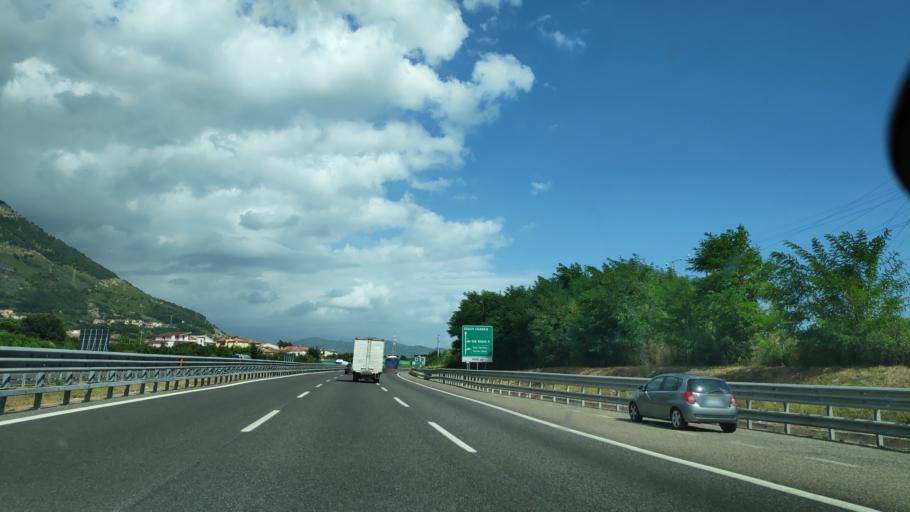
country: IT
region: Campania
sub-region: Provincia di Salerno
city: Piegolelle-San Bartolomeo
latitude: 40.6983
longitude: 14.8219
